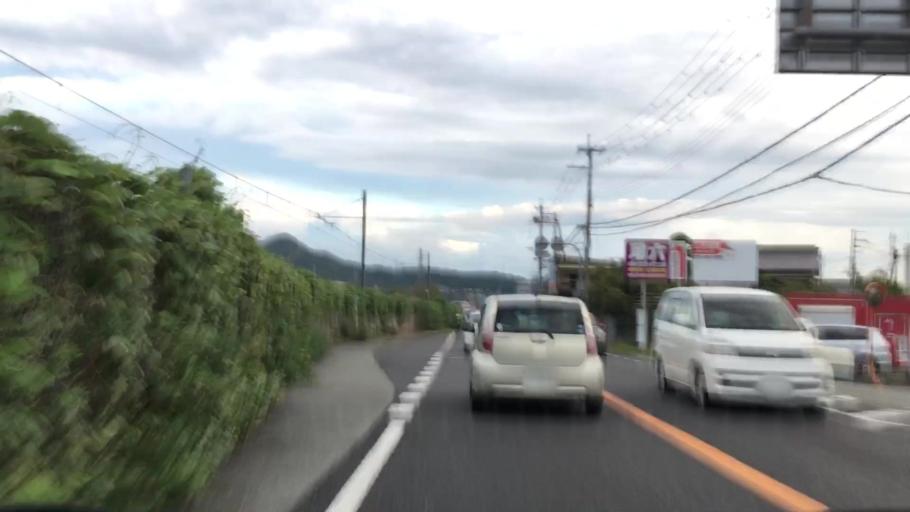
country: JP
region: Hyogo
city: Himeji
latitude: 34.8747
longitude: 134.7295
